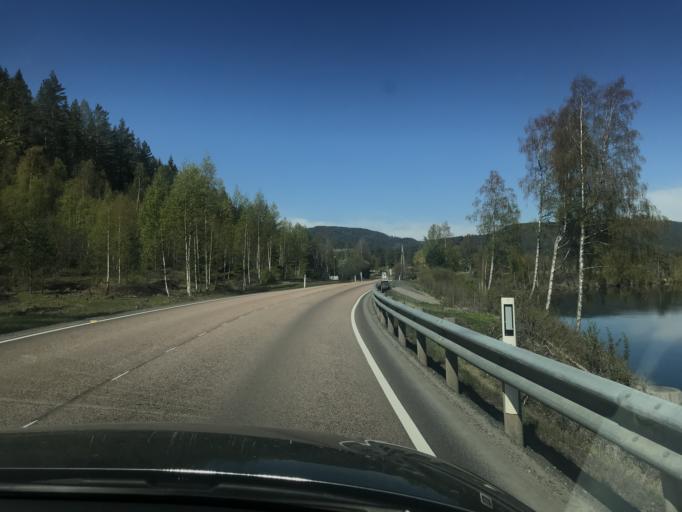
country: NO
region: Buskerud
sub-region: Kongsberg
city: Kongsberg
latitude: 59.7001
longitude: 9.6171
